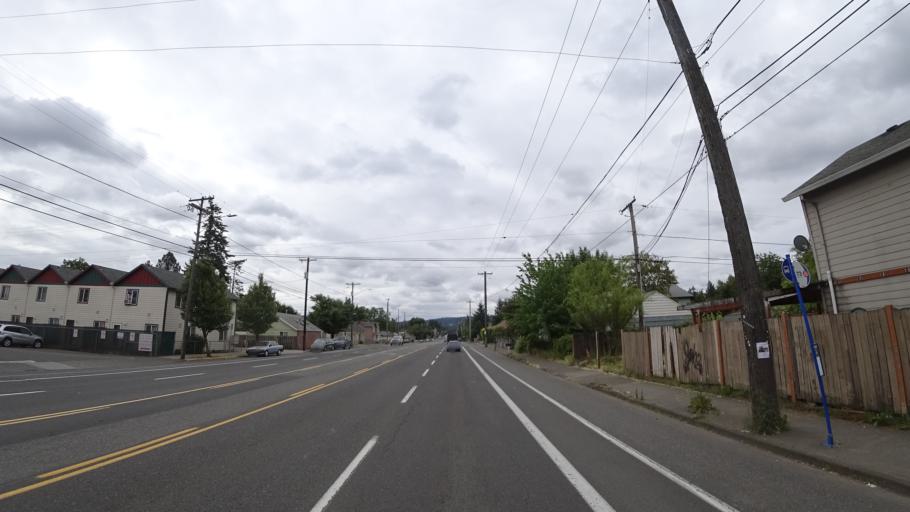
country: US
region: Oregon
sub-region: Multnomah County
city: Lents
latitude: 45.5007
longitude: -122.5378
